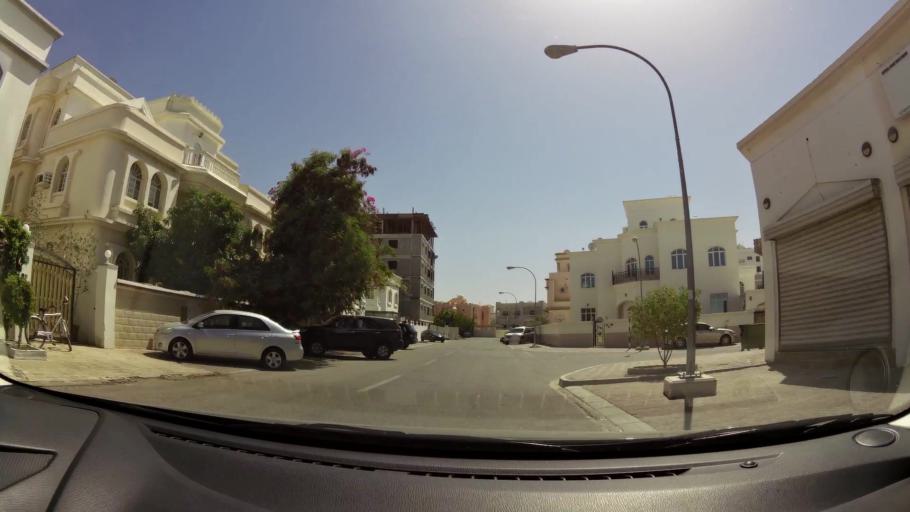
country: OM
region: Muhafazat Masqat
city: Bawshar
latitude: 23.5955
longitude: 58.3595
